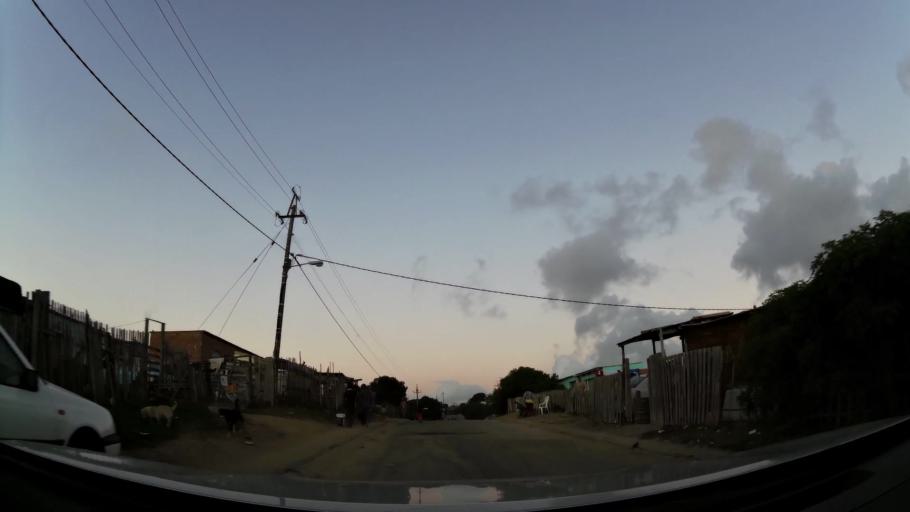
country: ZA
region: Western Cape
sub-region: Eden District Municipality
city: Knysna
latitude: -34.0258
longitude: 22.8167
